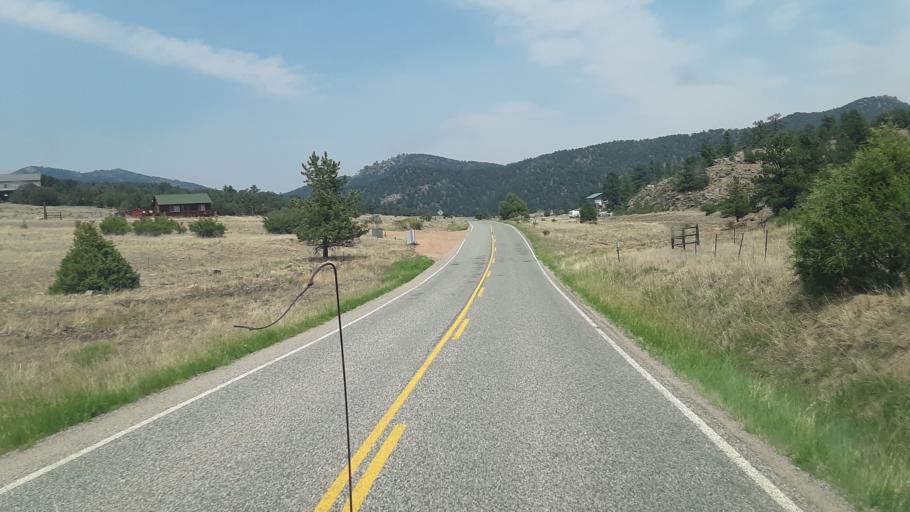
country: US
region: Colorado
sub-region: Fremont County
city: Canon City
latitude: 38.3676
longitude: -105.4614
